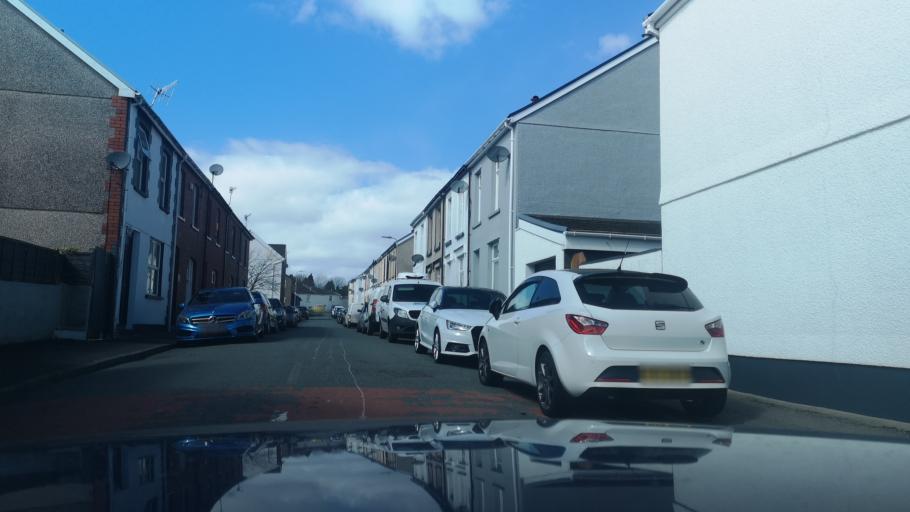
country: GB
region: Wales
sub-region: Merthyr Tydfil County Borough
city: Merthyr Tydfil
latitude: 51.7521
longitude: -3.3818
